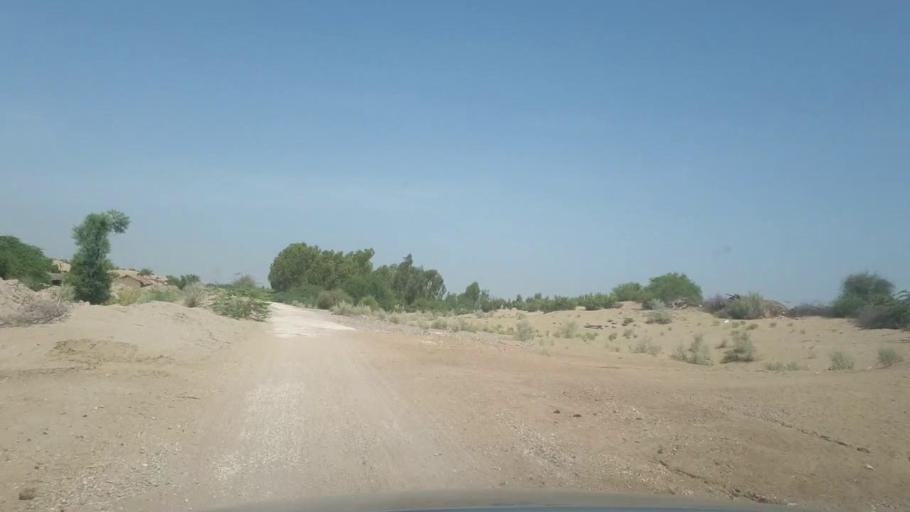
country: PK
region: Sindh
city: Khairpur
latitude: 27.3952
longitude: 69.0734
